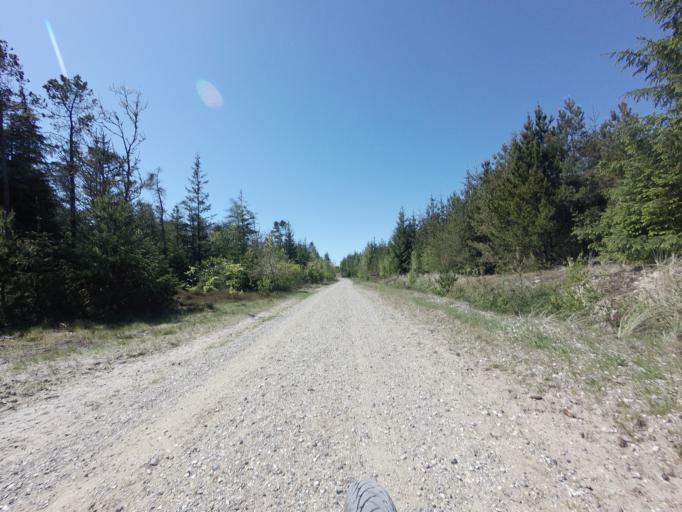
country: DK
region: North Denmark
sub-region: Jammerbugt Kommune
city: Pandrup
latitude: 57.2414
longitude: 9.5861
